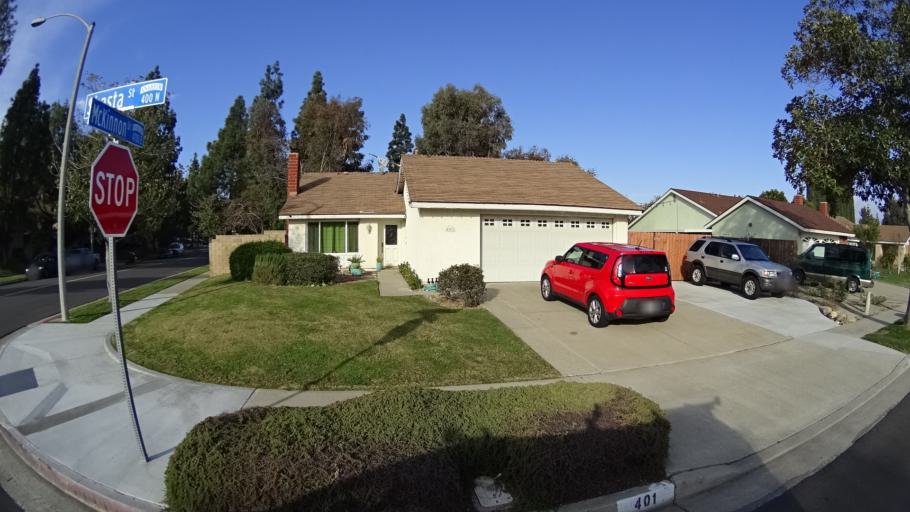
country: US
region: California
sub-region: Orange County
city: Yorba Linda
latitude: 33.8532
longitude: -117.8144
